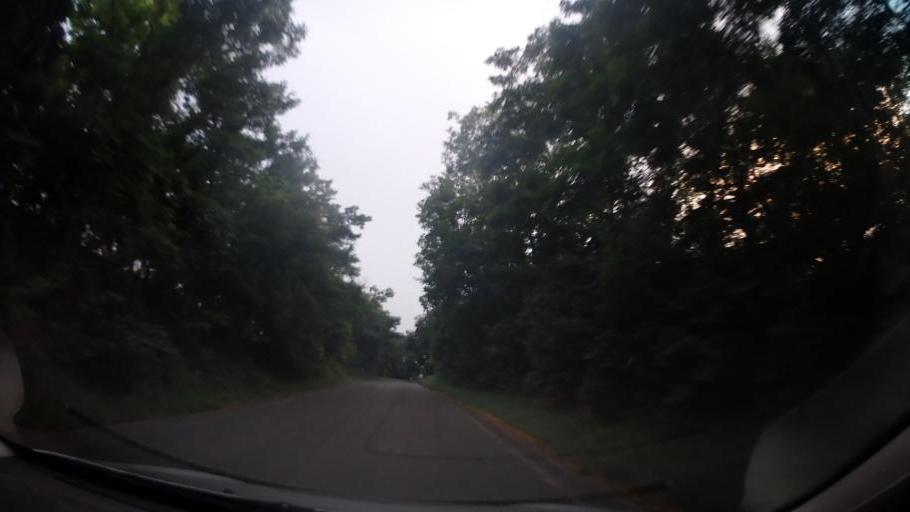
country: CZ
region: South Moravian
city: Dolni Kounice
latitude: 49.0732
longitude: 16.4902
